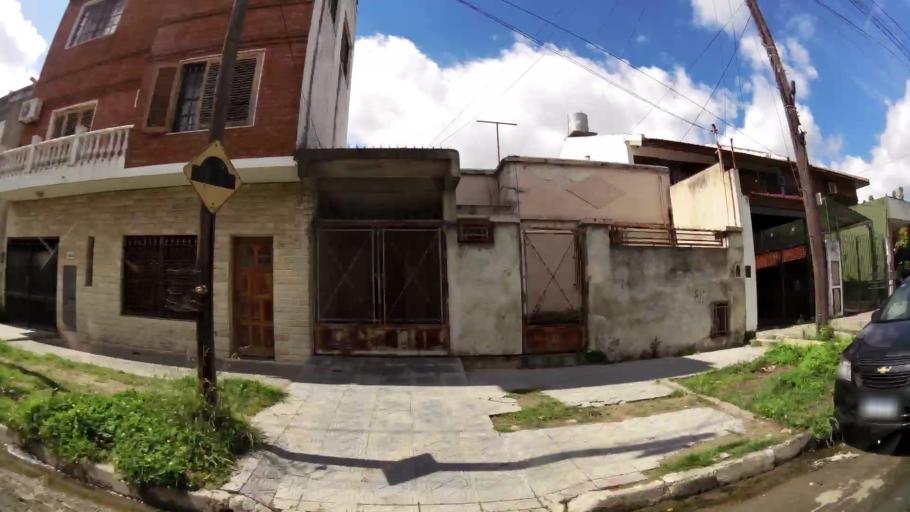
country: AR
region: Buenos Aires
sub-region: Partido de Lanus
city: Lanus
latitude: -34.6867
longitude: -58.4235
